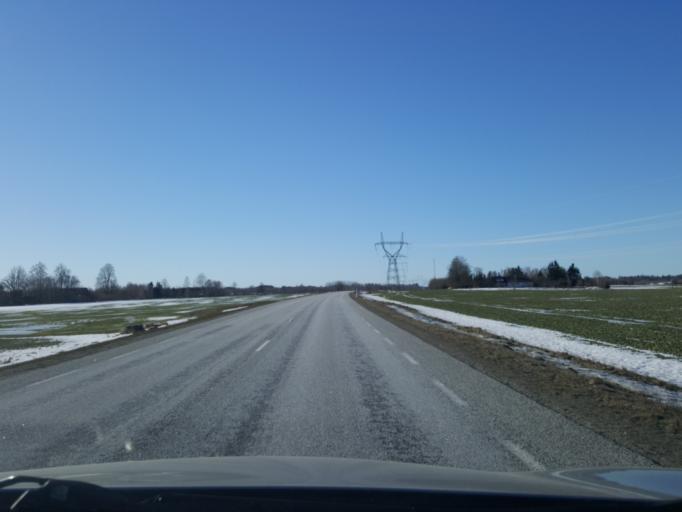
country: EE
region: Viljandimaa
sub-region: Viiratsi vald
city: Viiratsi
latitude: 58.3903
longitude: 25.6234
